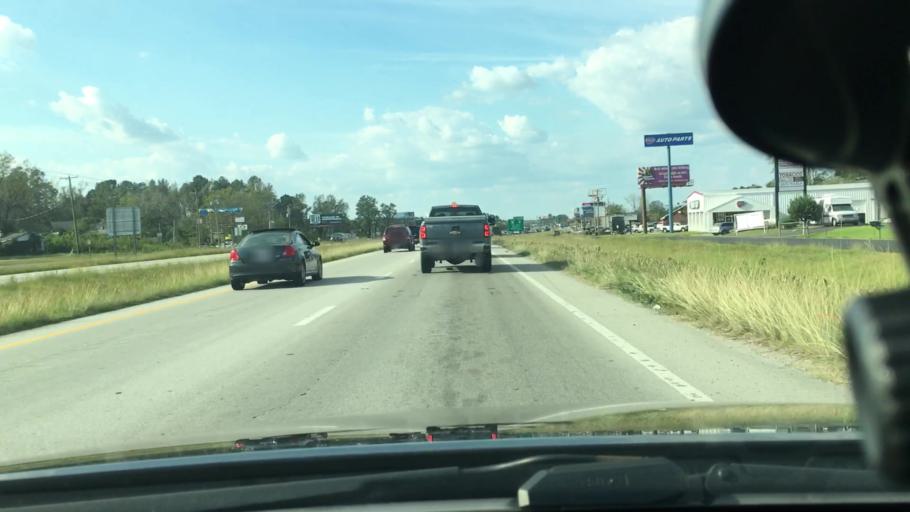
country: US
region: North Carolina
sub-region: Craven County
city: James City
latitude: 35.0768
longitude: -77.0289
